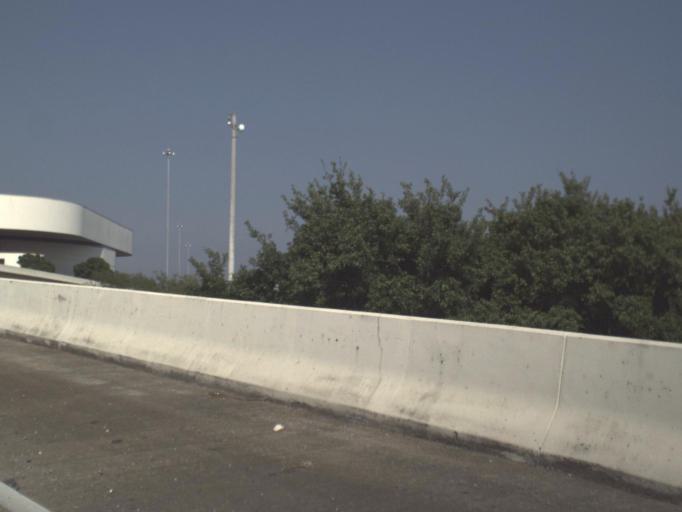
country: US
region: Florida
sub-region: Escambia County
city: Pensacola
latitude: 30.4152
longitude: -87.2117
